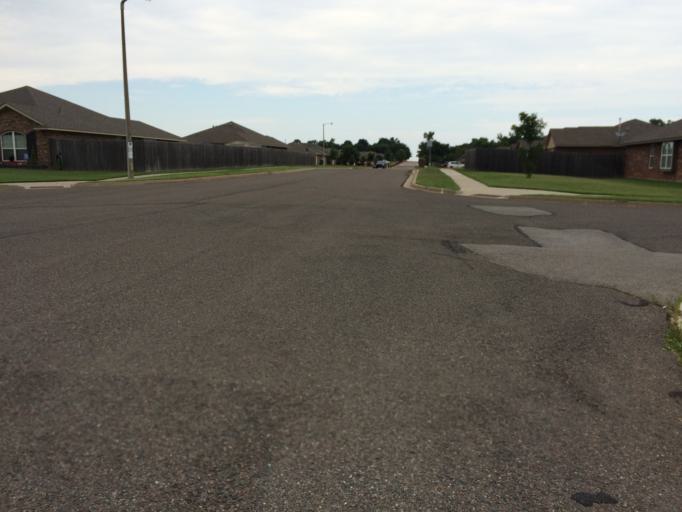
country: US
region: Oklahoma
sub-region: Cleveland County
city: Hall Park
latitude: 35.2477
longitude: -97.4188
